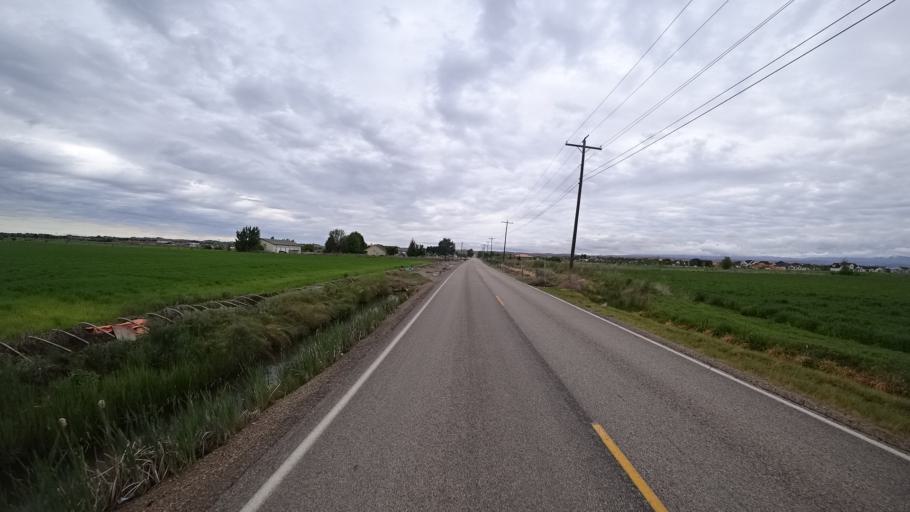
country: US
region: Idaho
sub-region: Ada County
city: Star
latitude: 43.6969
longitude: -116.4436
